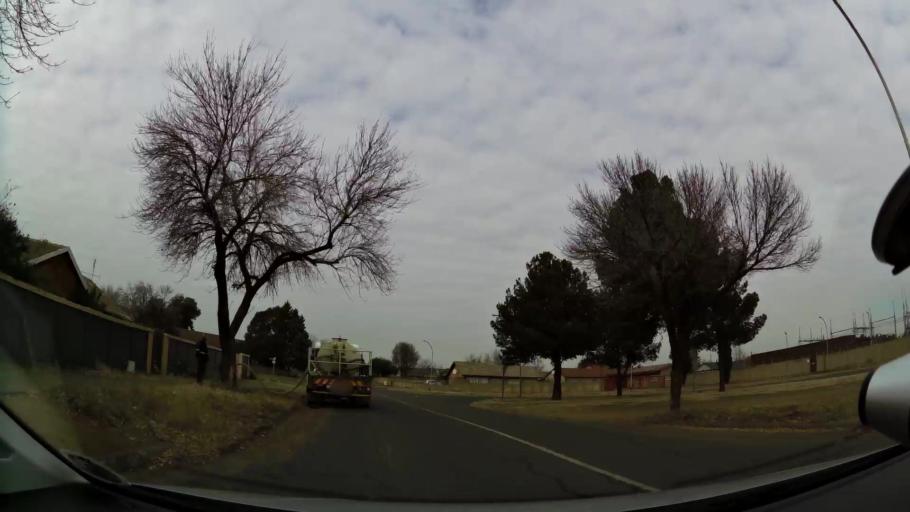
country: ZA
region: Orange Free State
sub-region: Mangaung Metropolitan Municipality
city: Bloemfontein
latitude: -29.1274
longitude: 26.1684
